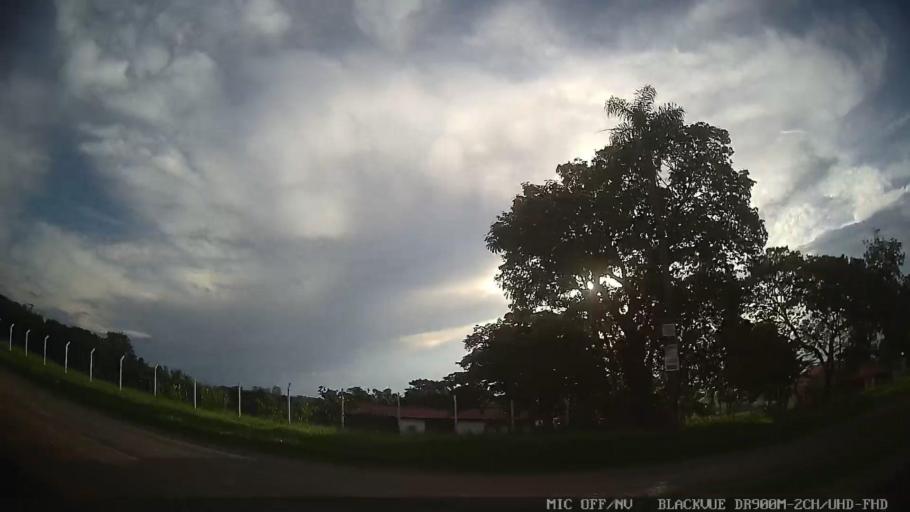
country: BR
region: Sao Paulo
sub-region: Boituva
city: Boituva
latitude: -23.1840
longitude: -47.6363
